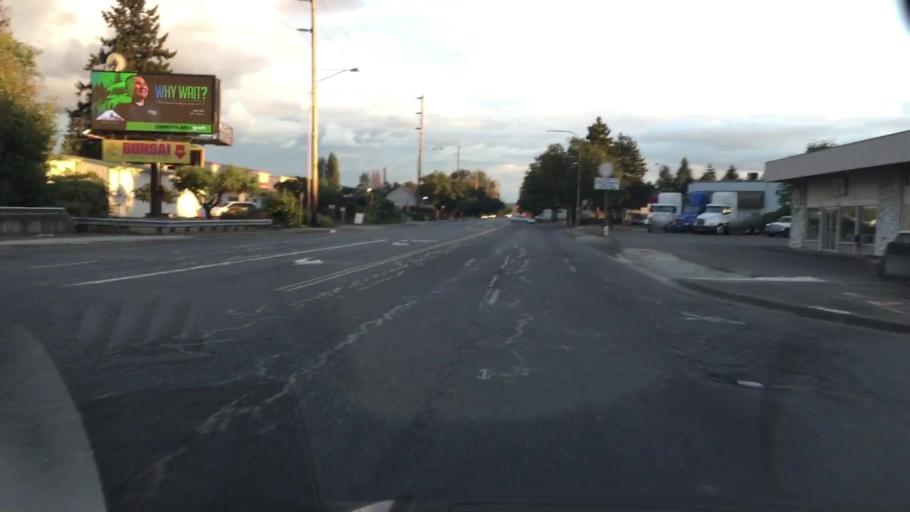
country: US
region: Washington
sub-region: King County
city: Kent
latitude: 47.4316
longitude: -122.2281
